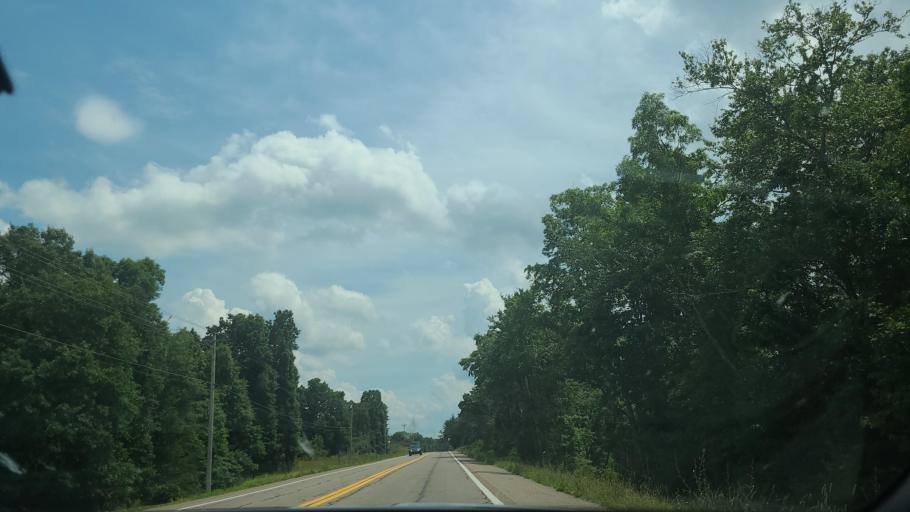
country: US
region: Tennessee
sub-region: Cumberland County
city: Lake Tansi
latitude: 35.8757
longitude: -85.0035
